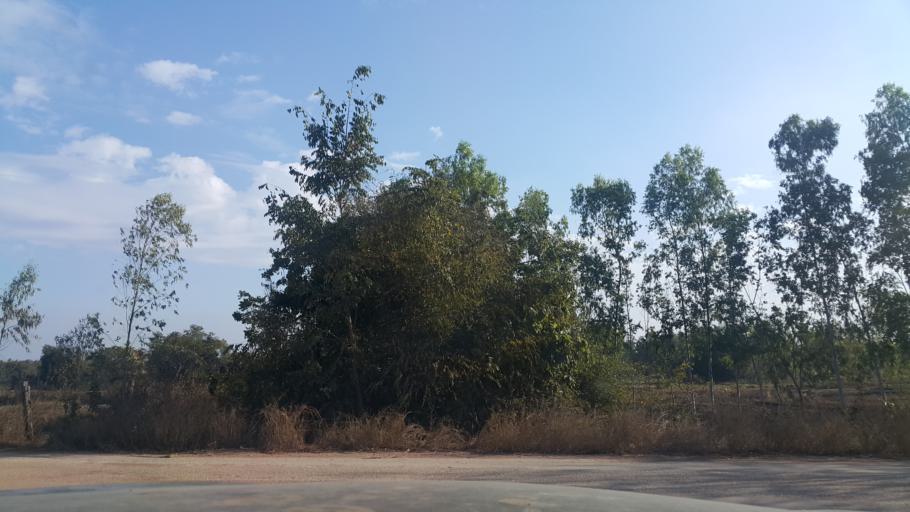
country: TH
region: Lampang
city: Hang Chat
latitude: 18.2741
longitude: 99.3562
